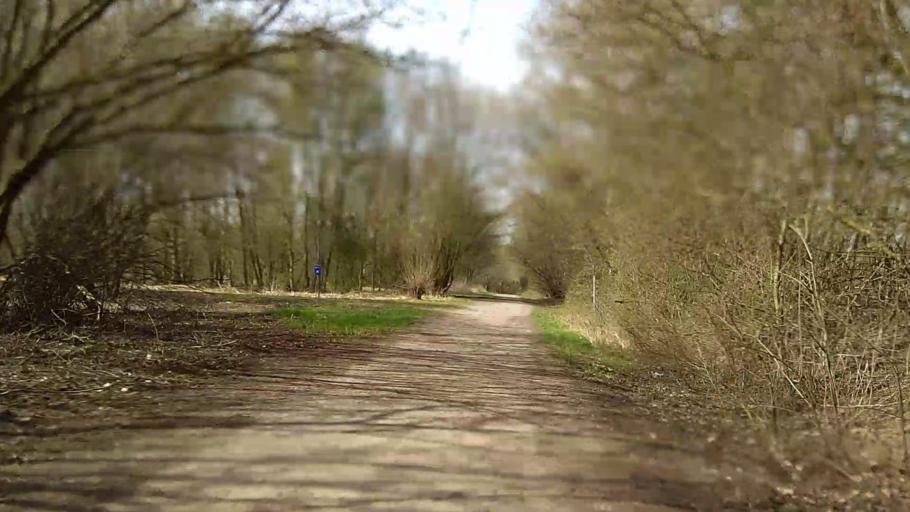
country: DE
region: North Rhine-Westphalia
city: Herten
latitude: 51.5675
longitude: 7.0983
